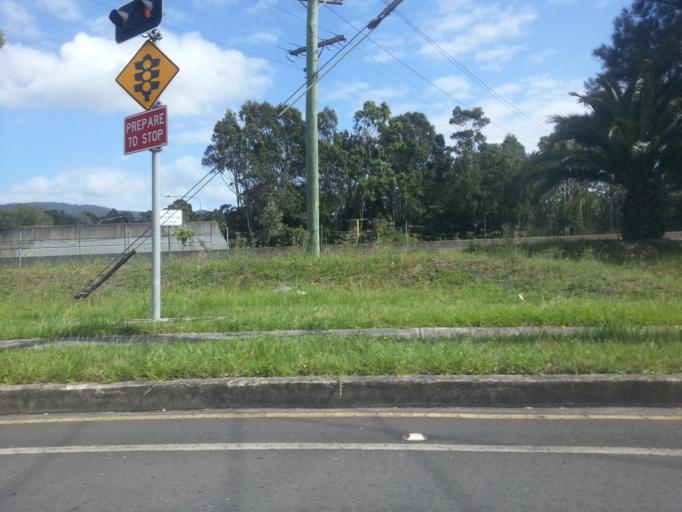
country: AU
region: New South Wales
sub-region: Wollongong
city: Gwynneville
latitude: -34.4127
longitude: 150.8861
